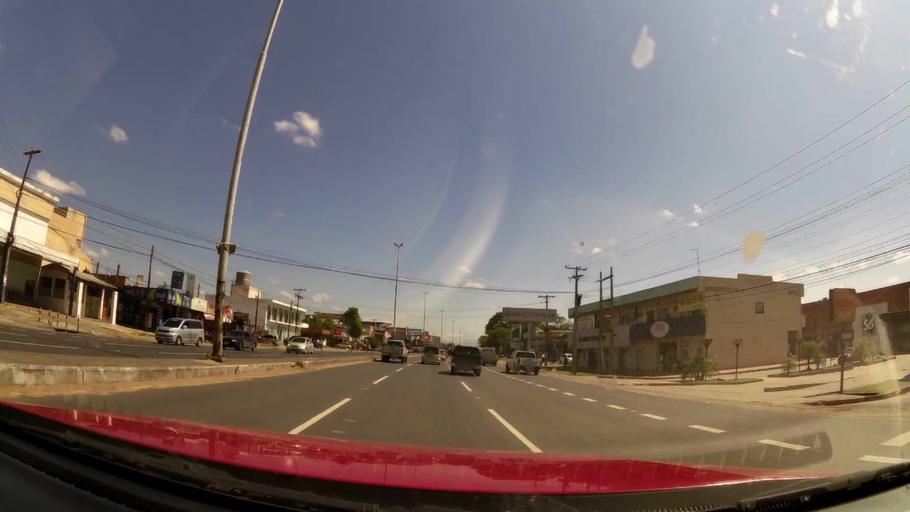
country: PY
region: Central
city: Colonia Mariano Roque Alonso
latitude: -25.2389
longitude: -57.5415
